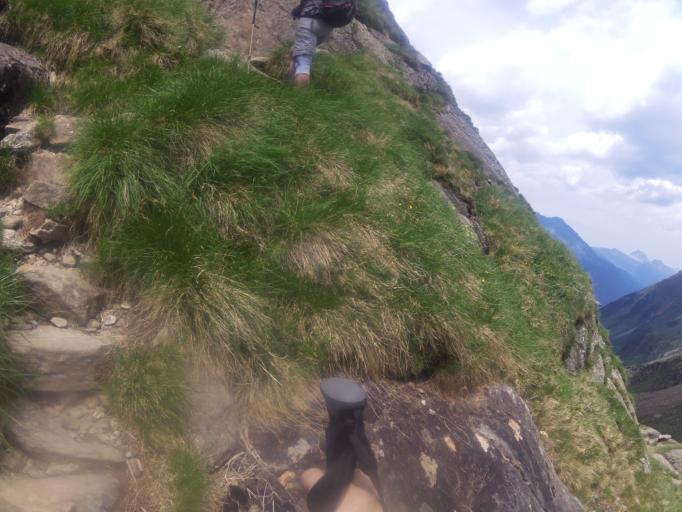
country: IT
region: Trentino-Alto Adige
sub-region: Bolzano
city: Racines
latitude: 46.9896
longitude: 11.2233
